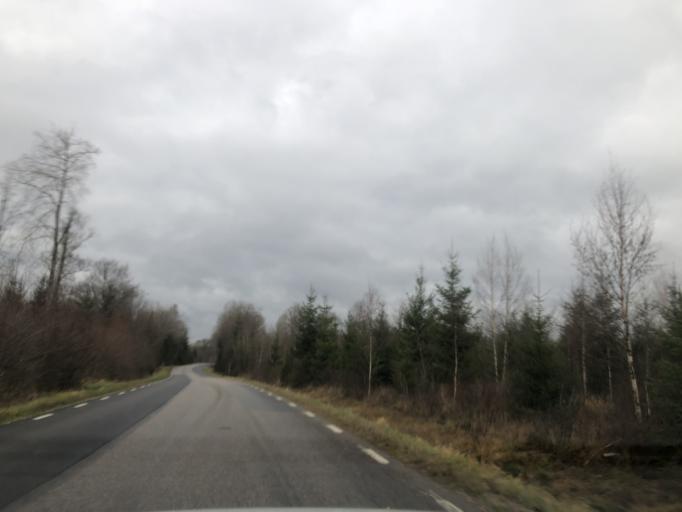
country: SE
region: Vaestra Goetaland
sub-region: Boras Kommun
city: Dalsjofors
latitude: 57.8206
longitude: 13.1958
